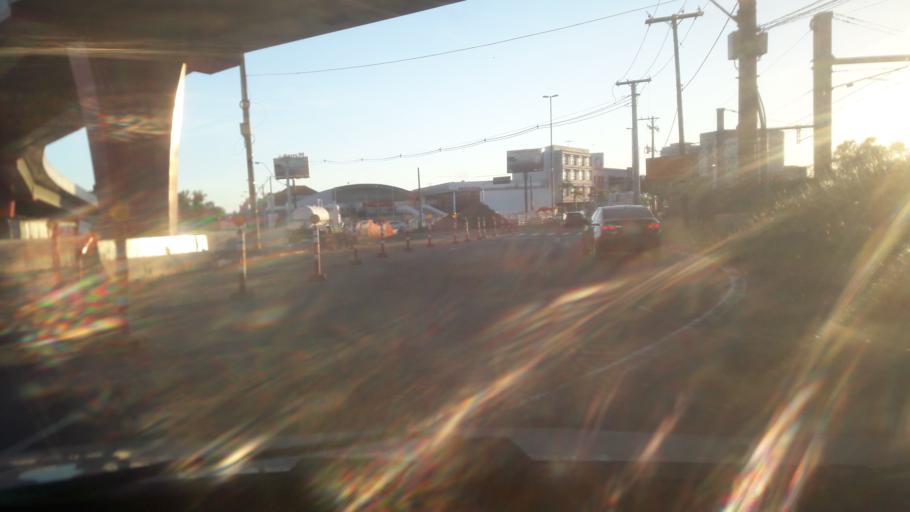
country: BR
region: Rio Grande do Sul
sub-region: Porto Alegre
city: Porto Alegre
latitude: -29.9959
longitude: -51.1897
